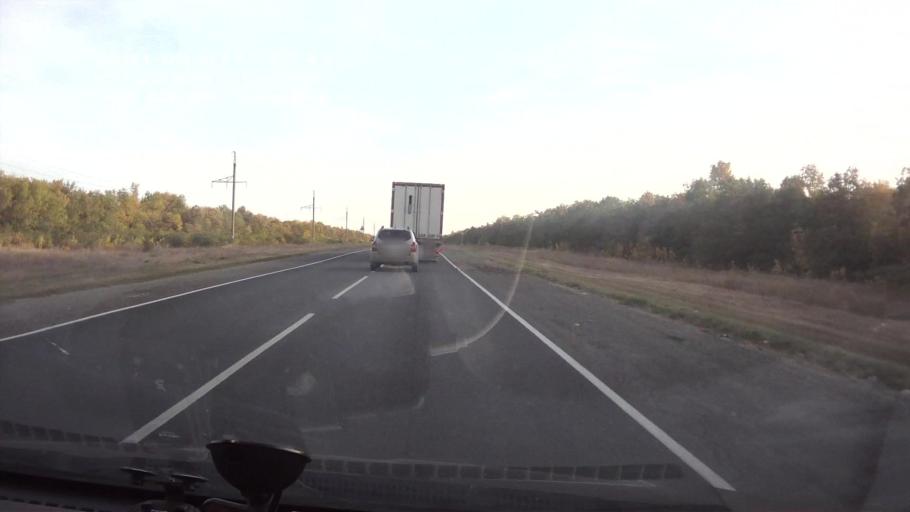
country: RU
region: Saratov
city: Krasnoarmeysk
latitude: 51.1267
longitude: 45.6506
